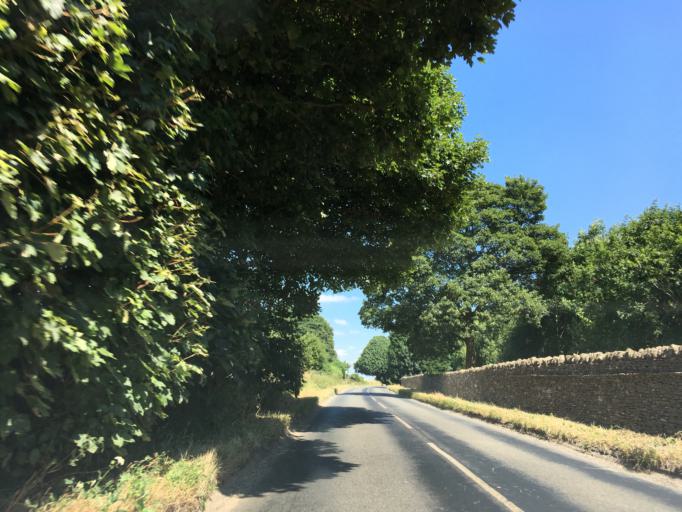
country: GB
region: England
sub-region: Gloucestershire
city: Stroud
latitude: 51.7534
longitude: -2.1703
